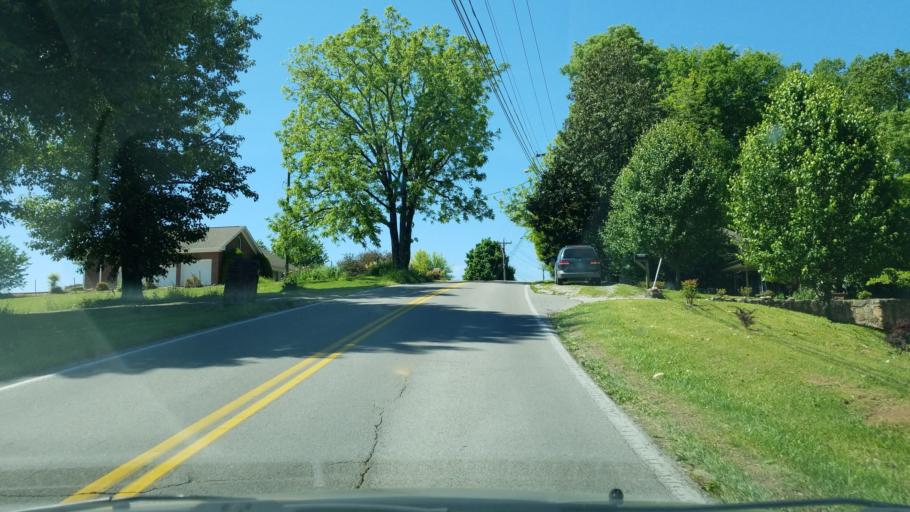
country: US
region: Tennessee
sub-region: Hamilton County
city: Middle Valley
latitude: 35.1526
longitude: -85.1921
